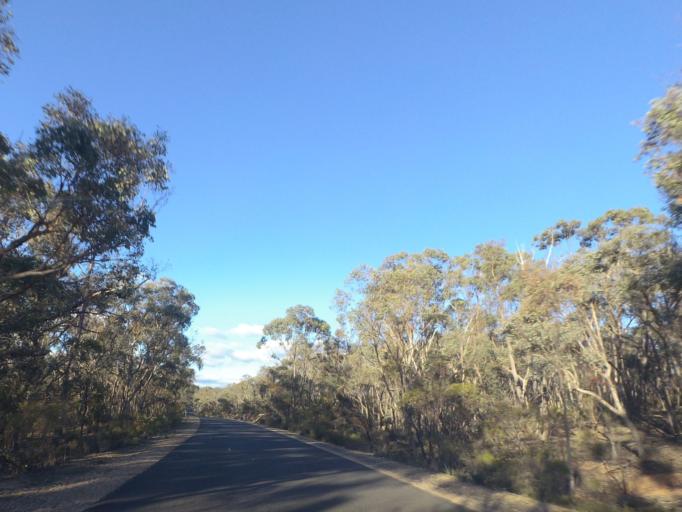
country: AU
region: Victoria
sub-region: Mount Alexander
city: Castlemaine
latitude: -37.1563
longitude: 144.2266
